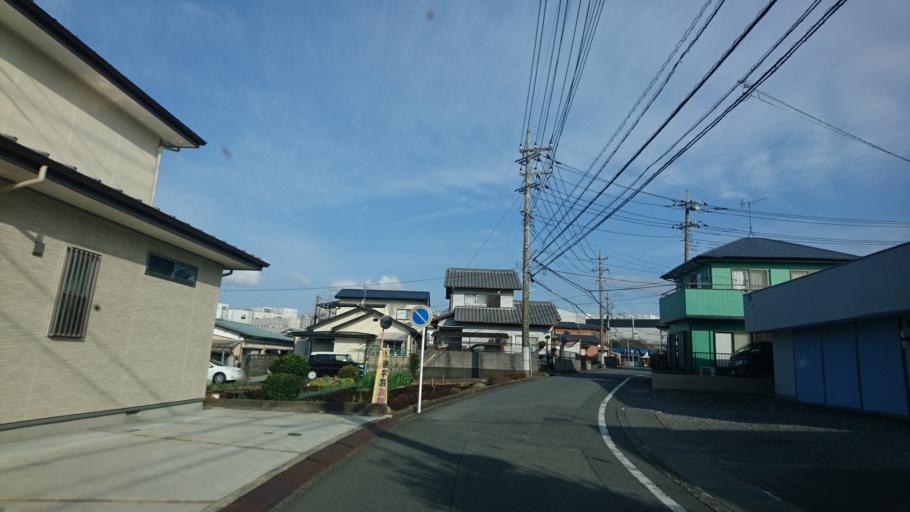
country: JP
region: Shizuoka
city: Fujinomiya
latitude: 35.2414
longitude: 138.6157
